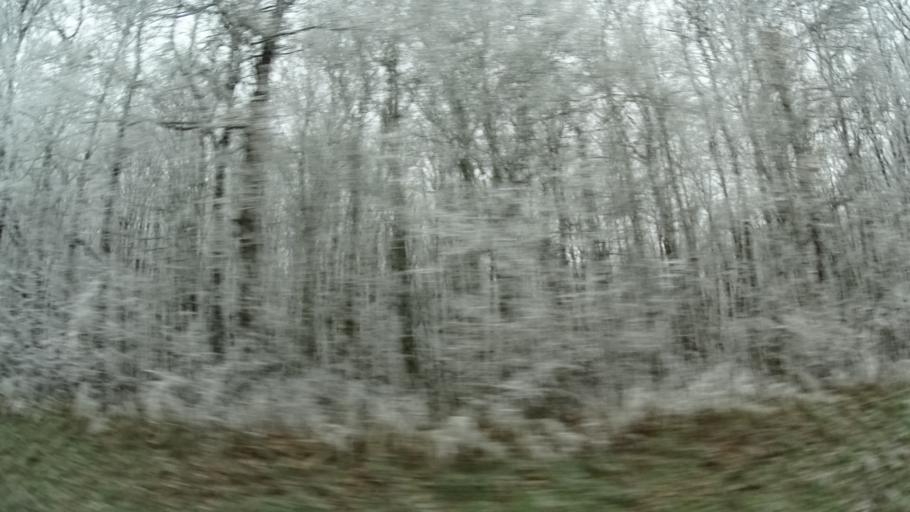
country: DE
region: Bavaria
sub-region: Regierungsbezirk Unterfranken
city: Hassfurt
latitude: 50.0202
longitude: 10.4943
